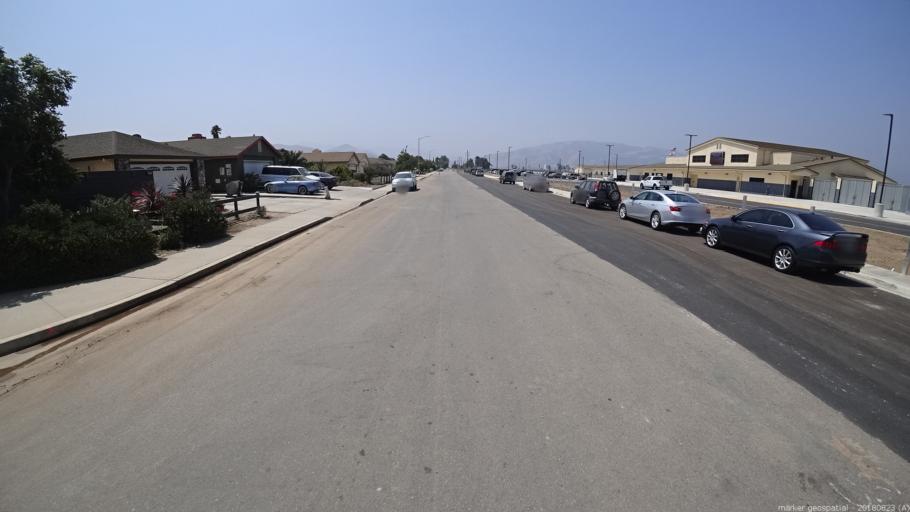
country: US
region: California
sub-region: Monterey County
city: Greenfield
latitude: 36.3185
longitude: -121.2555
